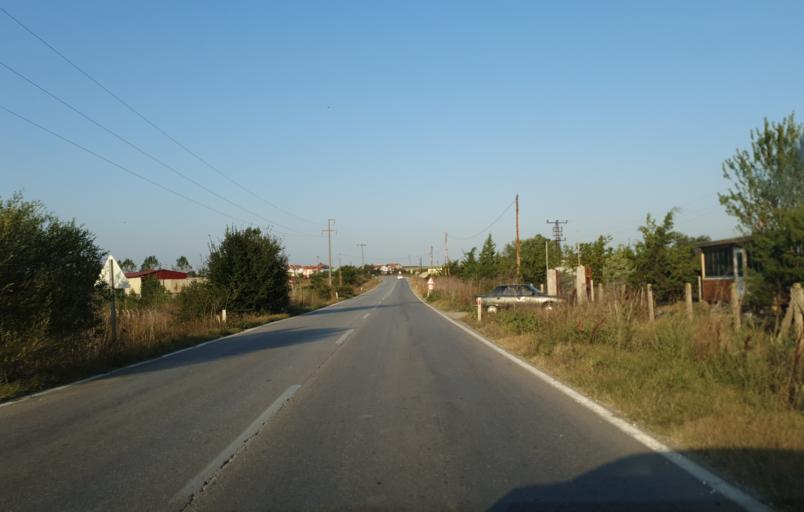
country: TR
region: Tekirdag
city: Saray
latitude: 41.4308
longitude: 27.8917
